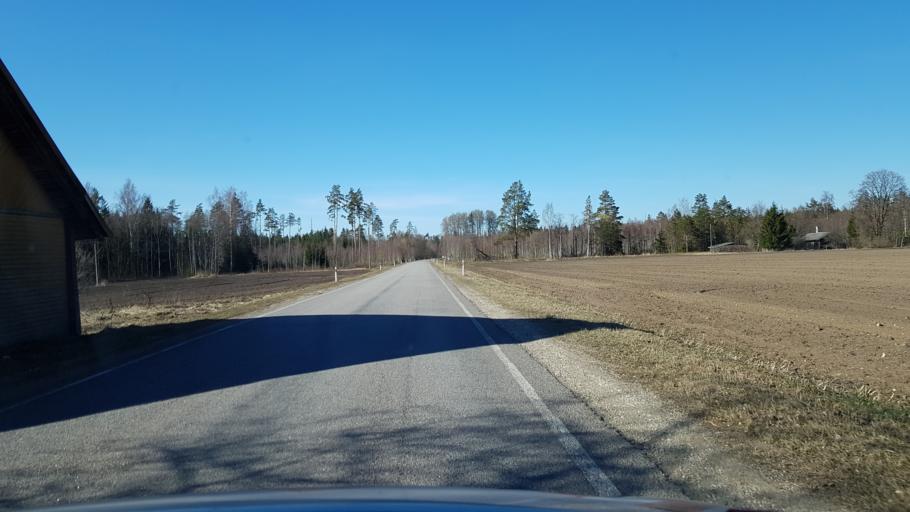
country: EE
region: Laeaene-Virumaa
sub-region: Vinni vald
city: Vinni
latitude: 59.2427
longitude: 26.6911
